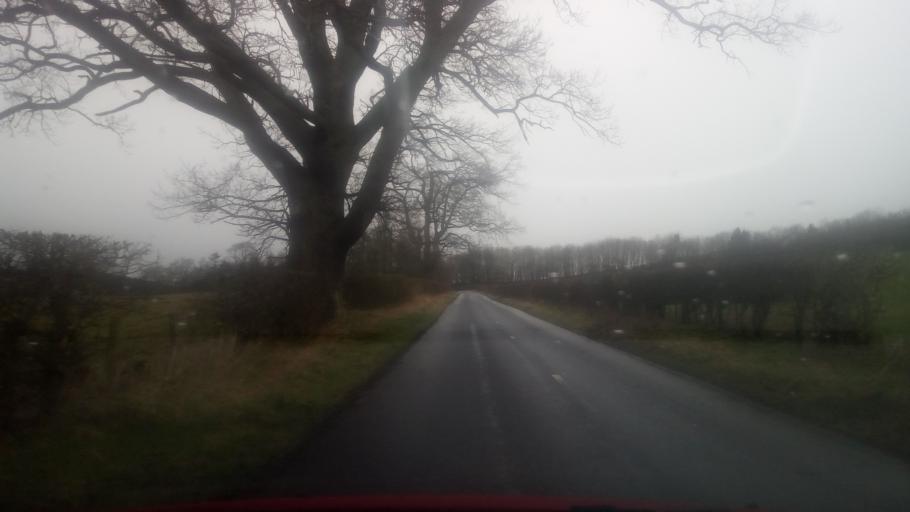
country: GB
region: Scotland
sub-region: The Scottish Borders
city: Earlston
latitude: 55.6275
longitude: -2.6702
